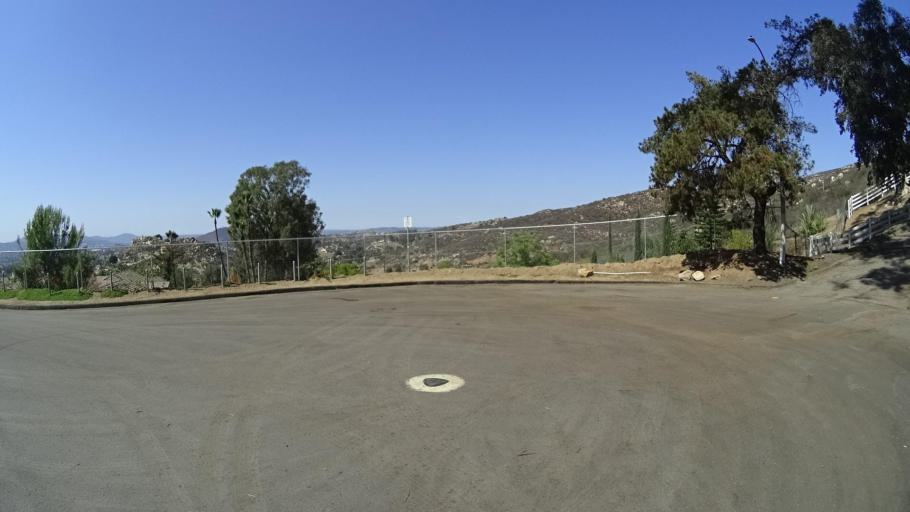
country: US
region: California
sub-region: San Diego County
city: Granite Hills
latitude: 32.8054
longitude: -116.8948
